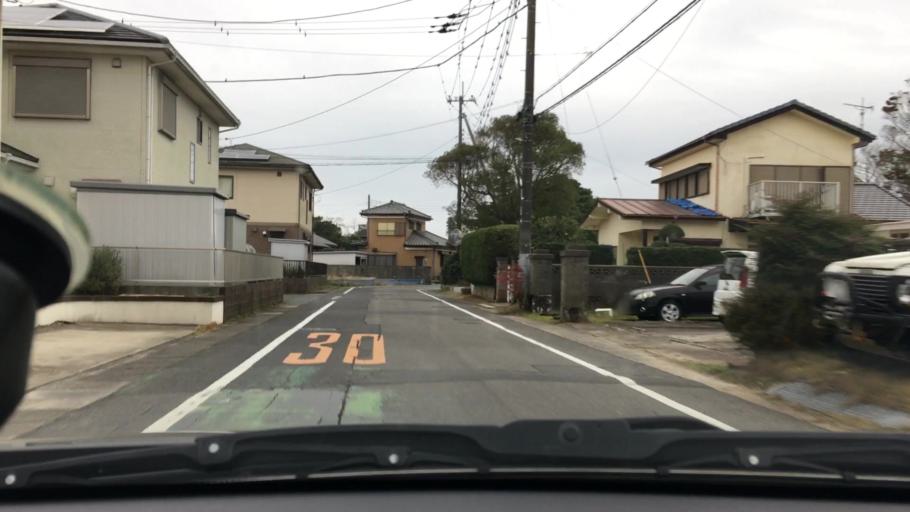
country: JP
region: Chiba
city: Omigawa
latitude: 35.8698
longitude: 140.6723
